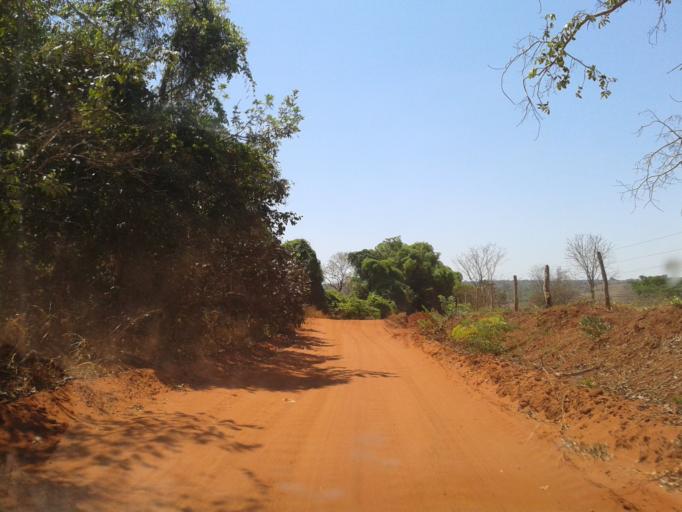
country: BR
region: Minas Gerais
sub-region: Ituiutaba
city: Ituiutaba
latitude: -19.0682
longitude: -49.3284
